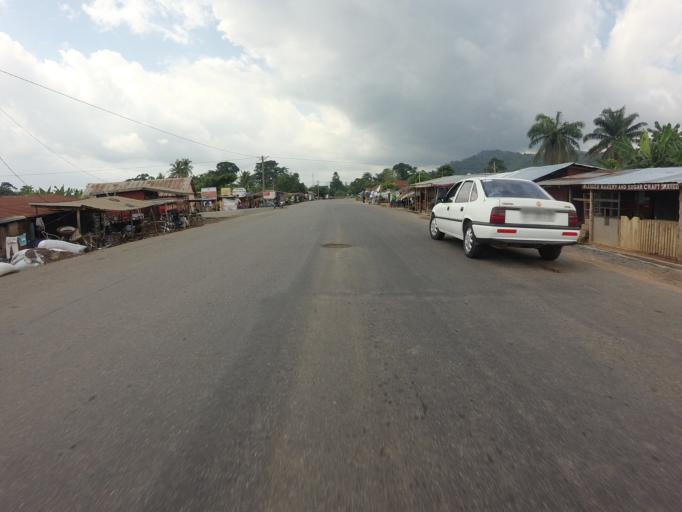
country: GH
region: Volta
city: Kpandu
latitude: 6.8947
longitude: 0.4306
